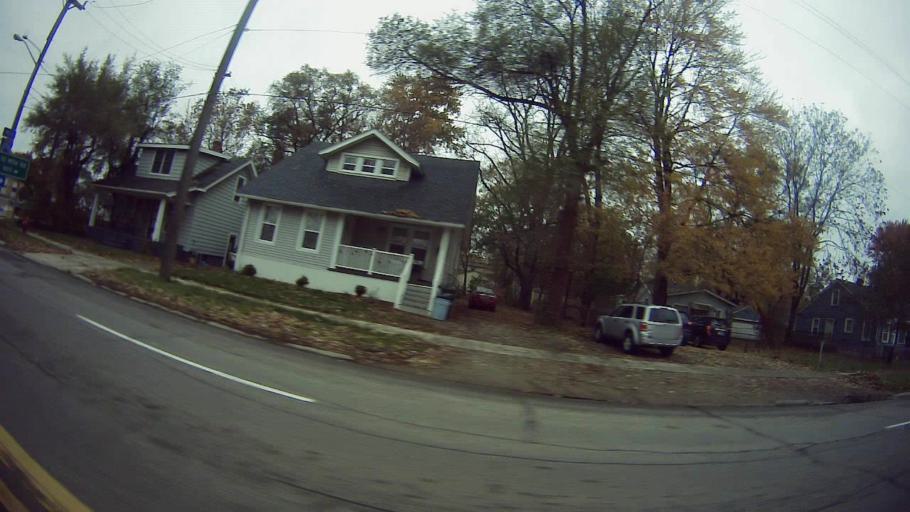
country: US
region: Michigan
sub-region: Oakland County
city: Pleasant Ridge
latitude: 42.4768
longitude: -83.1238
